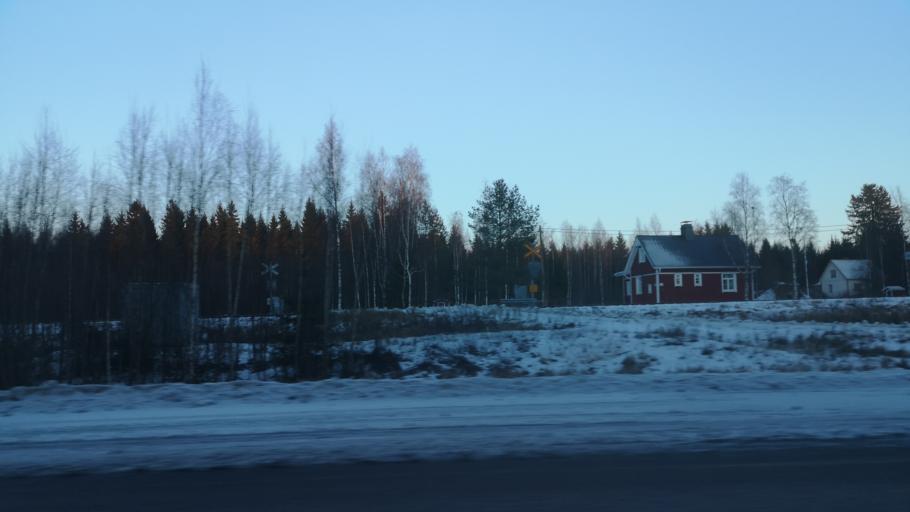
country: FI
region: Southern Savonia
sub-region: Savonlinna
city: Sulkava
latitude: 61.9380
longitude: 28.5335
